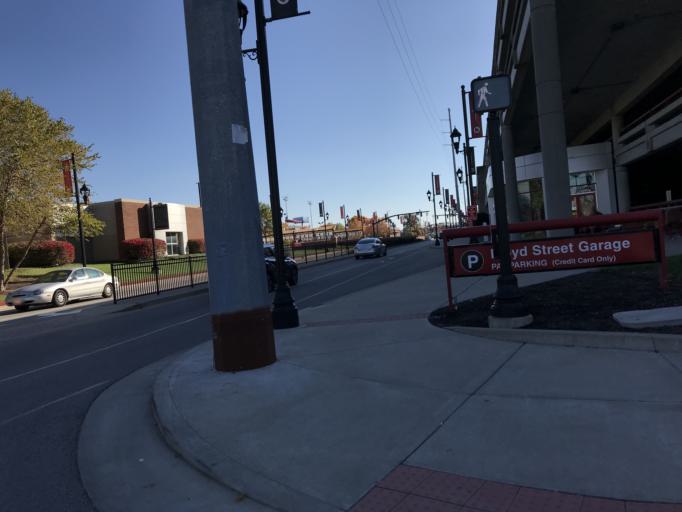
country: US
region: Kentucky
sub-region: Jefferson County
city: Audubon Park
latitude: 38.2170
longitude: -85.7548
